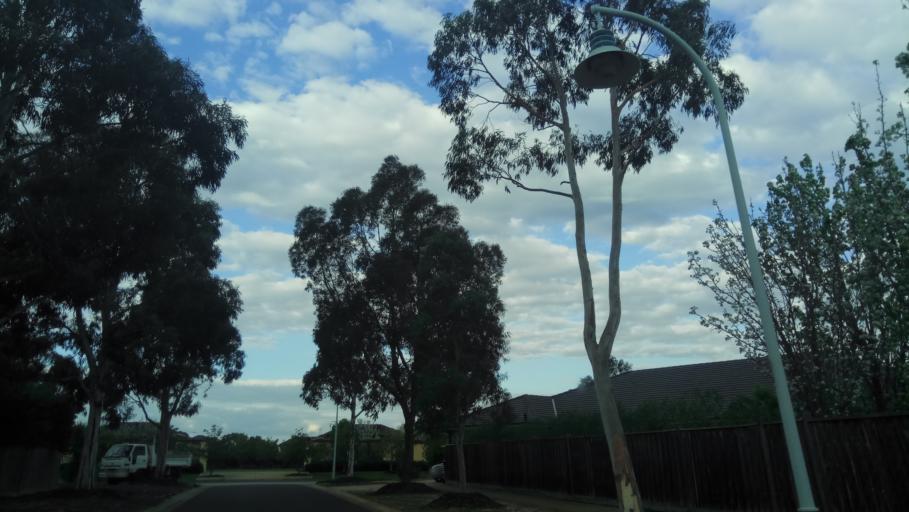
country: AU
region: Victoria
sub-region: Hobsons Bay
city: Altona Meadows
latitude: -37.8888
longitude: 144.7721
